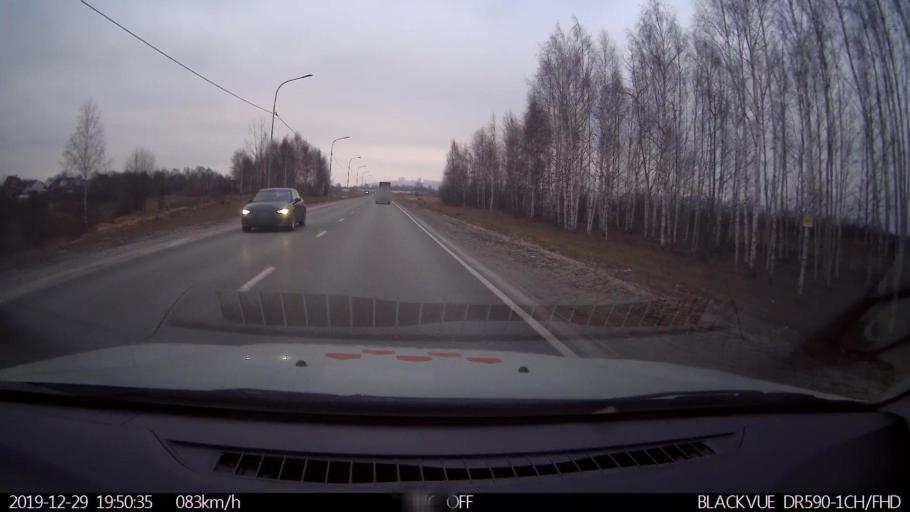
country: RU
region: Nizjnij Novgorod
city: Bor
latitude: 56.3664
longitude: 44.0298
